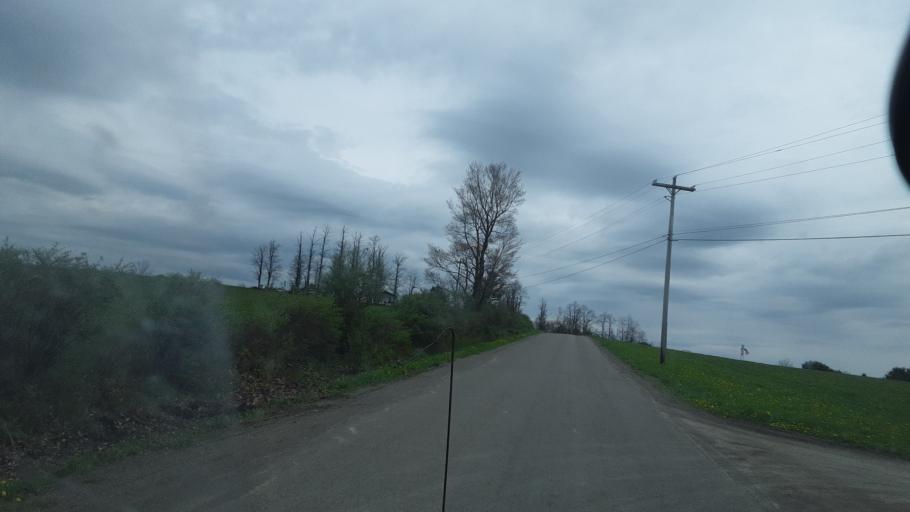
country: US
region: New York
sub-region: Steuben County
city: Addison
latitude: 42.0922
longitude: -77.2877
